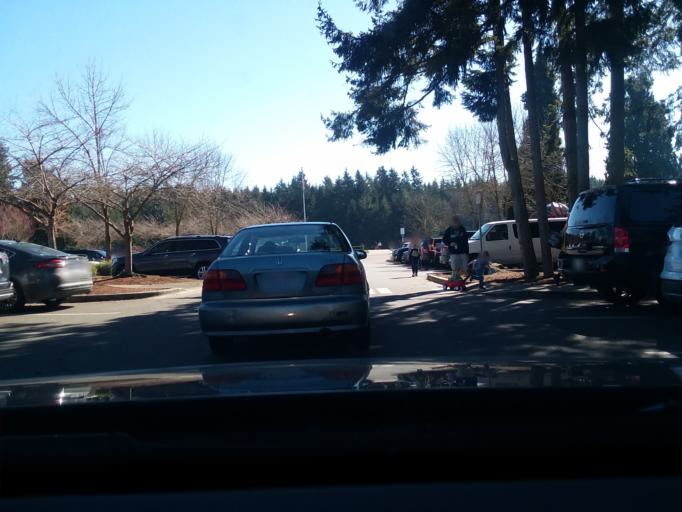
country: US
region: Washington
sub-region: Pierce County
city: Puyallup
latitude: 47.1629
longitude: -122.2867
